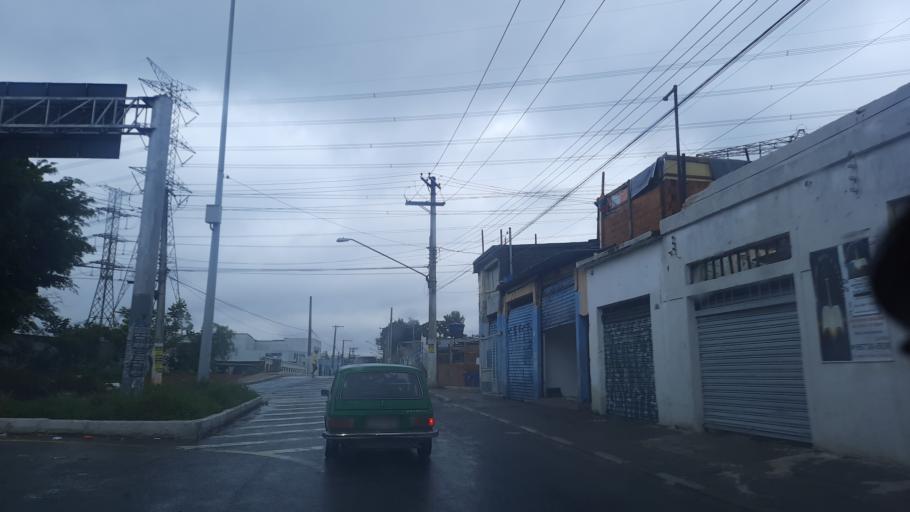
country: BR
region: Sao Paulo
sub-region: Guarulhos
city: Guarulhos
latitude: -23.4628
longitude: -46.5681
